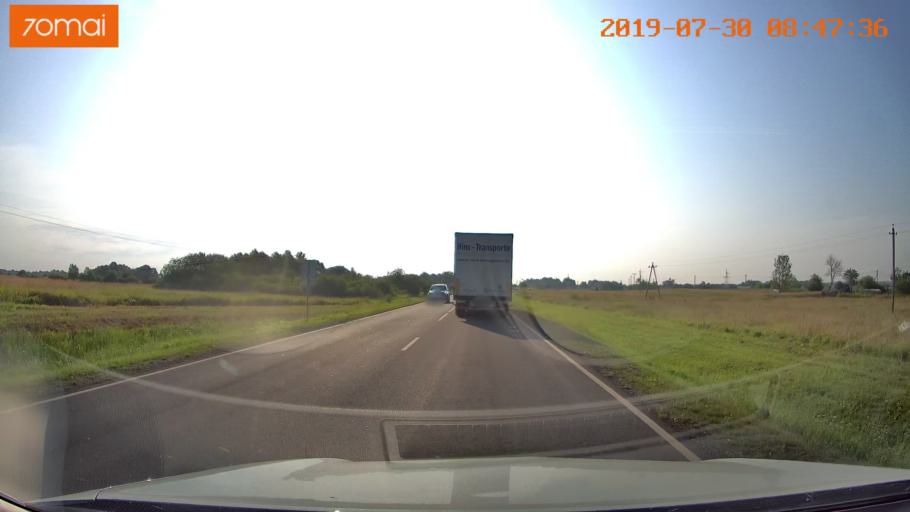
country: RU
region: Kaliningrad
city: Chernyakhovsk
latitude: 54.6212
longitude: 21.8949
